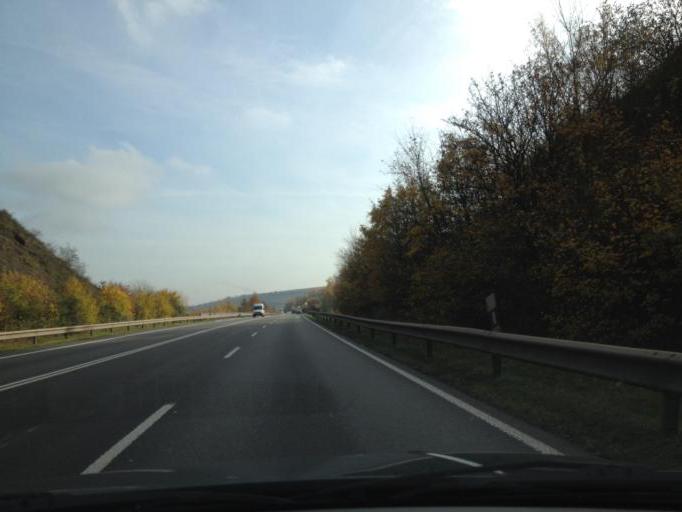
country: DE
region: Rheinland-Pfalz
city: Albersweiler
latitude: 49.2143
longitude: 8.0245
